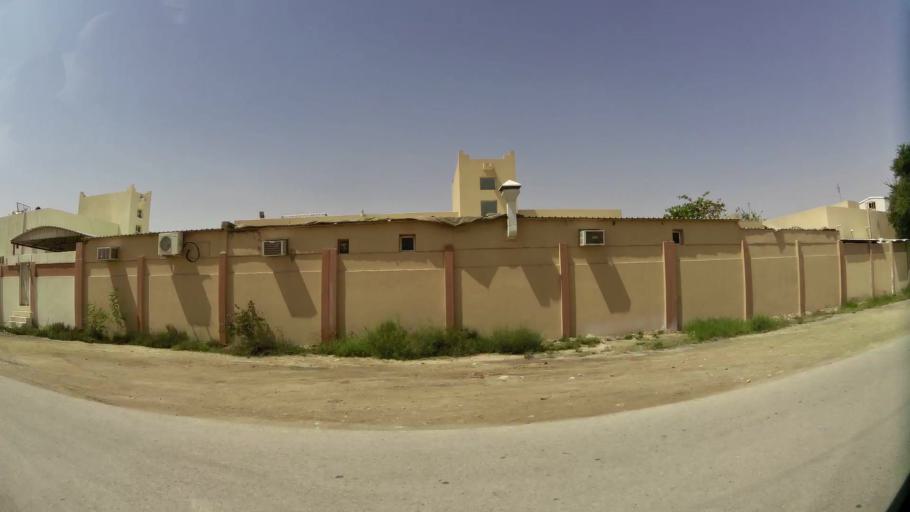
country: QA
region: Baladiyat Umm Salal
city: Umm Salal Muhammad
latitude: 25.3760
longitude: 51.4756
